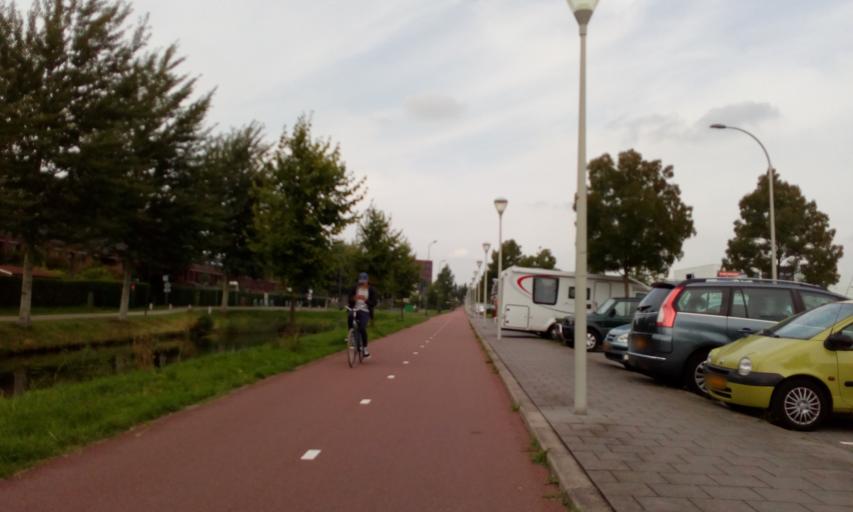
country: NL
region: South Holland
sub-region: Gemeente Den Haag
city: Ypenburg
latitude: 52.0515
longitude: 4.3982
